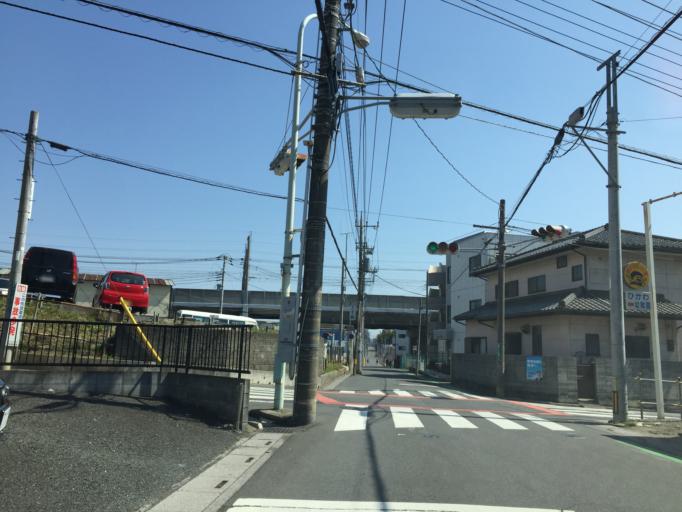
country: JP
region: Saitama
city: Yono
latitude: 35.8578
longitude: 139.6333
